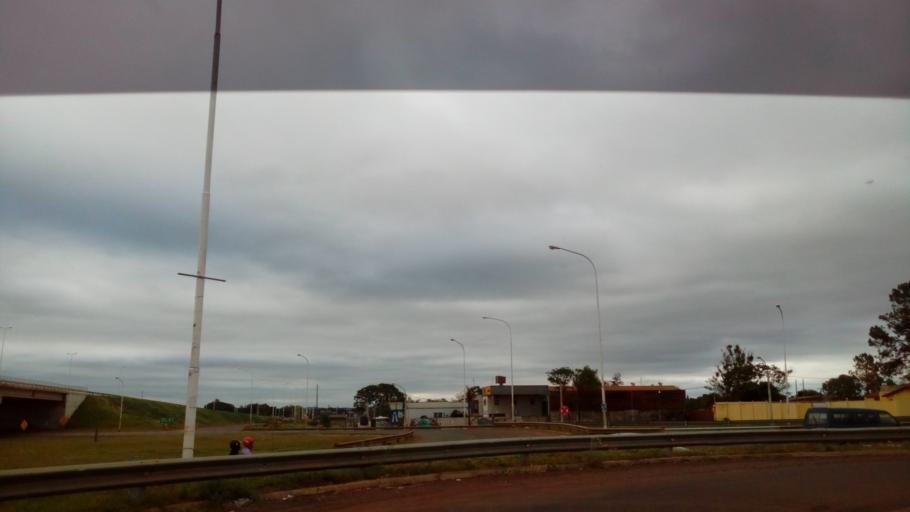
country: AR
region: Misiones
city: Garupa
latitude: -27.4540
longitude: -55.8608
